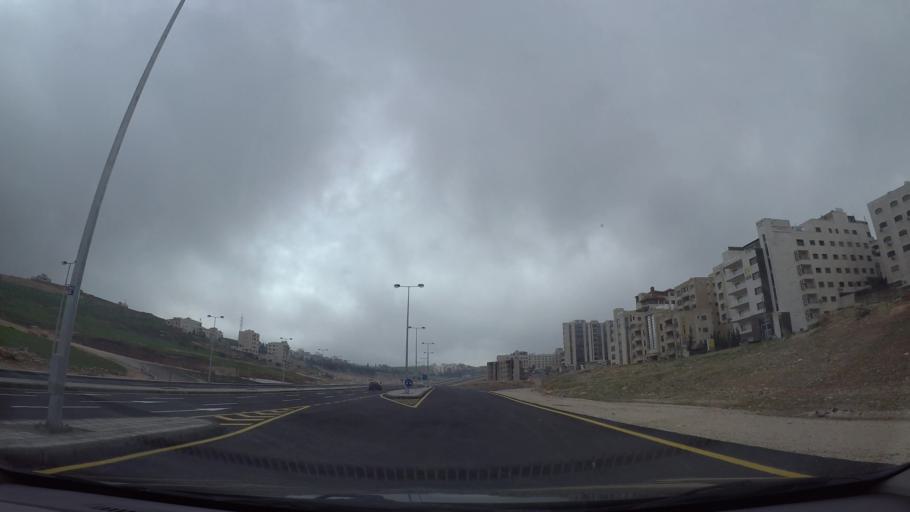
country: JO
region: Amman
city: Wadi as Sir
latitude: 31.9343
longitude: 35.8653
